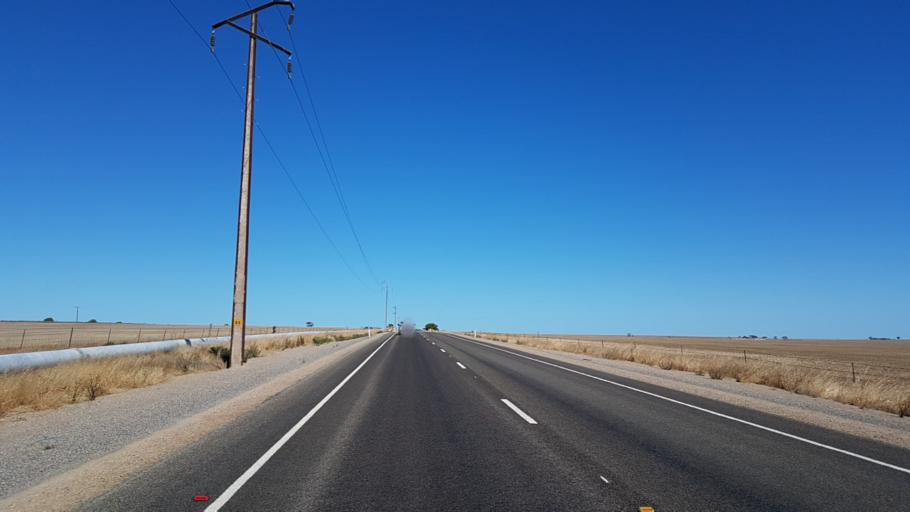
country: AU
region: South Australia
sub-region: Copper Coast
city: Kadina
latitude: -34.0433
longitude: 137.9343
